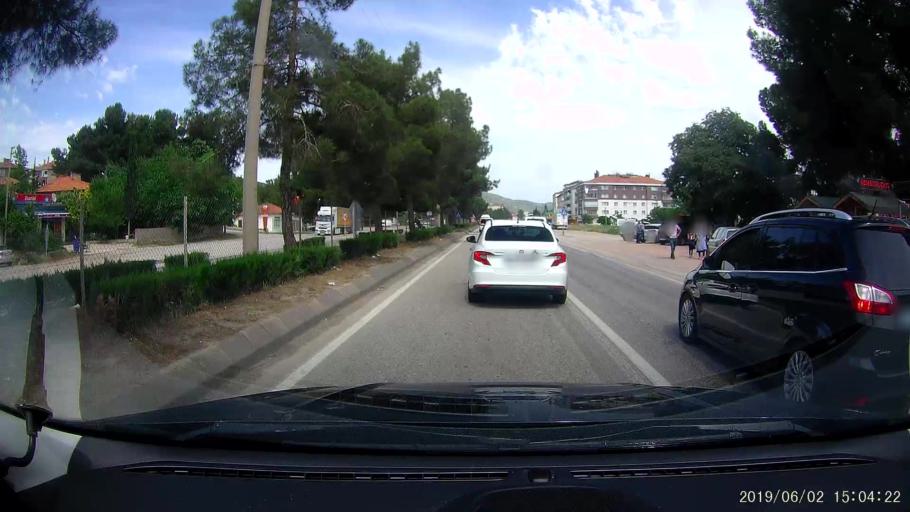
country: TR
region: Corum
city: Osmancik
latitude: 40.9793
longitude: 34.7927
